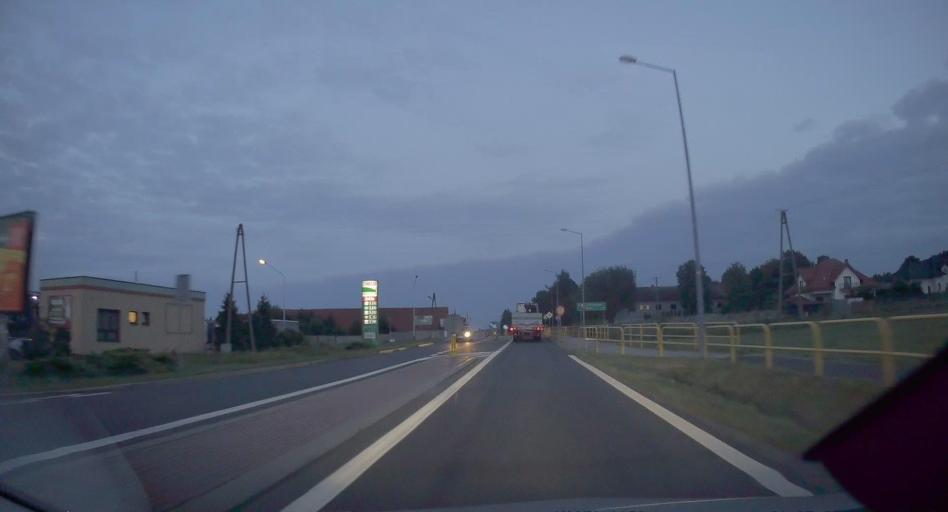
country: PL
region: Silesian Voivodeship
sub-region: Powiat klobucki
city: Opatow
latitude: 50.9304
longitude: 18.8587
